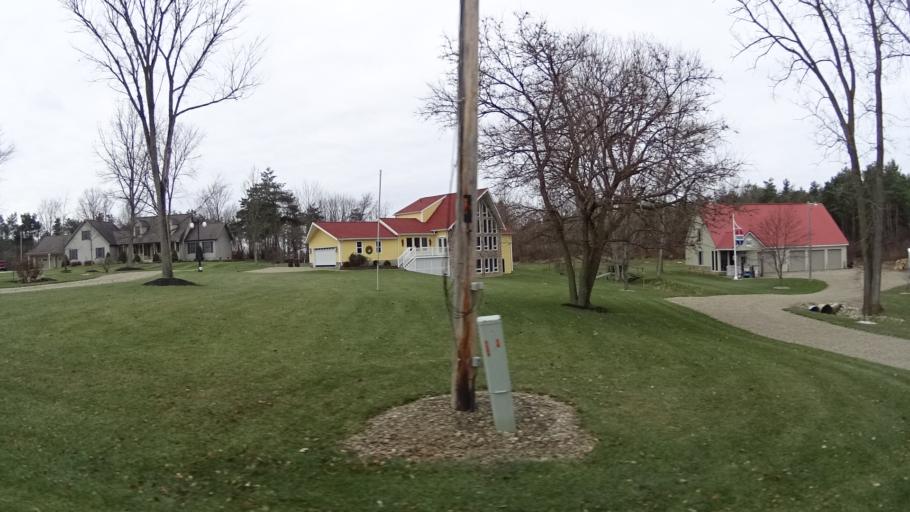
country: US
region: Ohio
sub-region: Lorain County
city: Wellington
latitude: 41.1323
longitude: -82.2693
